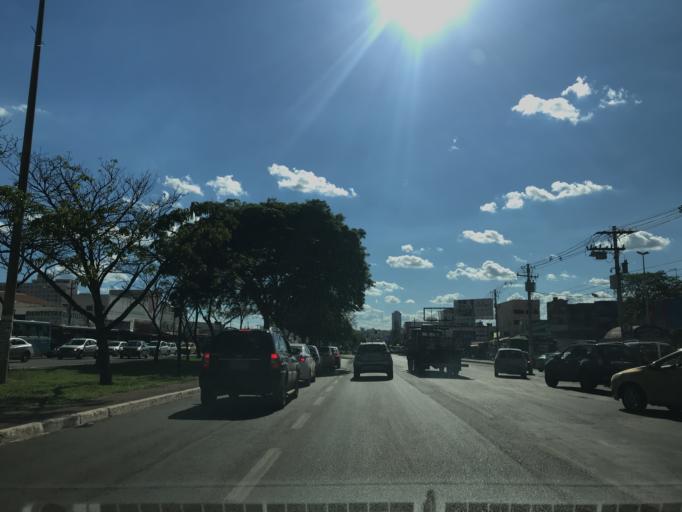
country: BR
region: Federal District
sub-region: Brasilia
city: Brasilia
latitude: -15.8031
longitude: -48.0685
